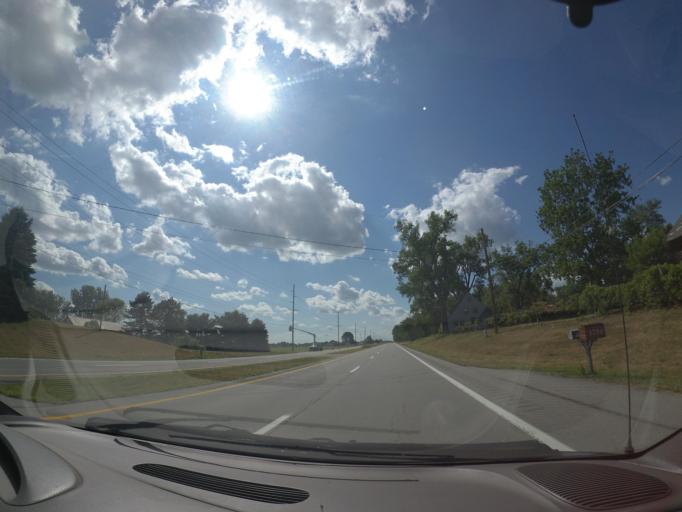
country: US
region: Ohio
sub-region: Sandusky County
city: Mount Carmel
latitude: 41.2973
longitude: -82.9275
